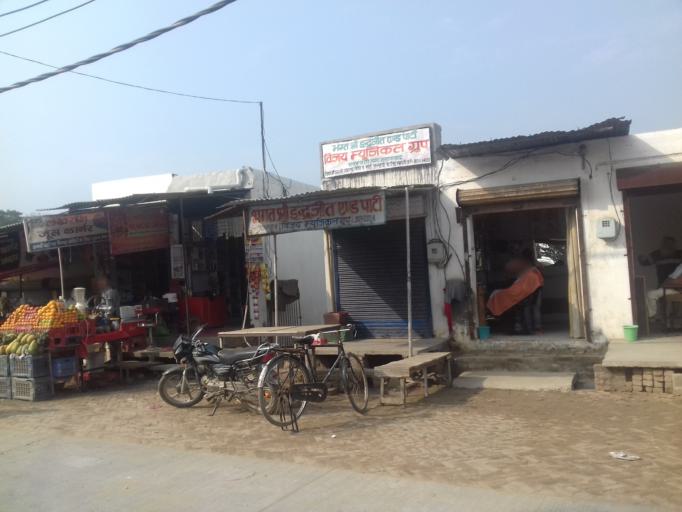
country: IN
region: Haryana
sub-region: Yamunanagar
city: Mustafabad
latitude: 30.2003
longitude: 77.1444
